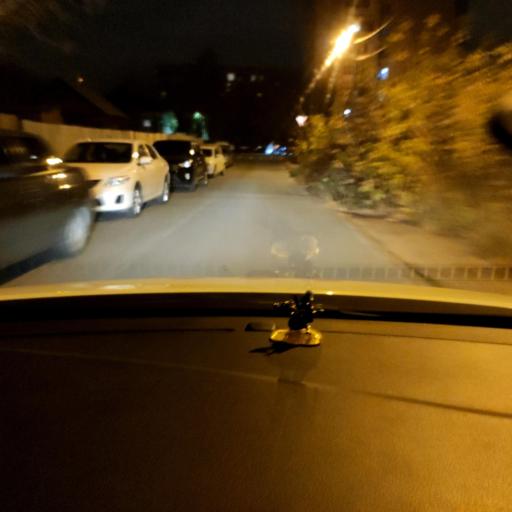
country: RU
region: Tatarstan
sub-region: Gorod Kazan'
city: Kazan
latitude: 55.7967
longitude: 49.0667
